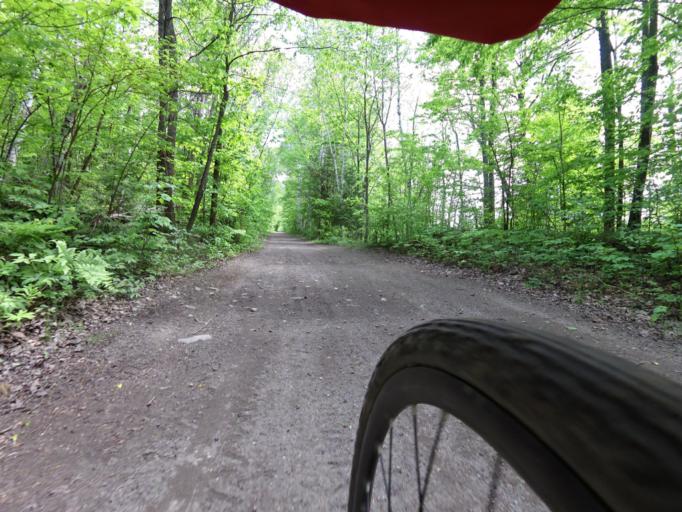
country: CA
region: Ontario
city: Renfrew
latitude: 45.2005
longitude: -76.6855
